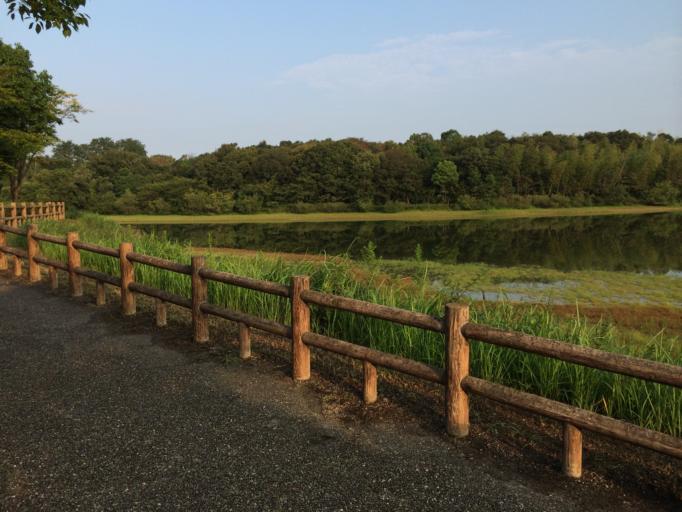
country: JP
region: Aichi
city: Chiryu
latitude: 35.0524
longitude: 137.0562
